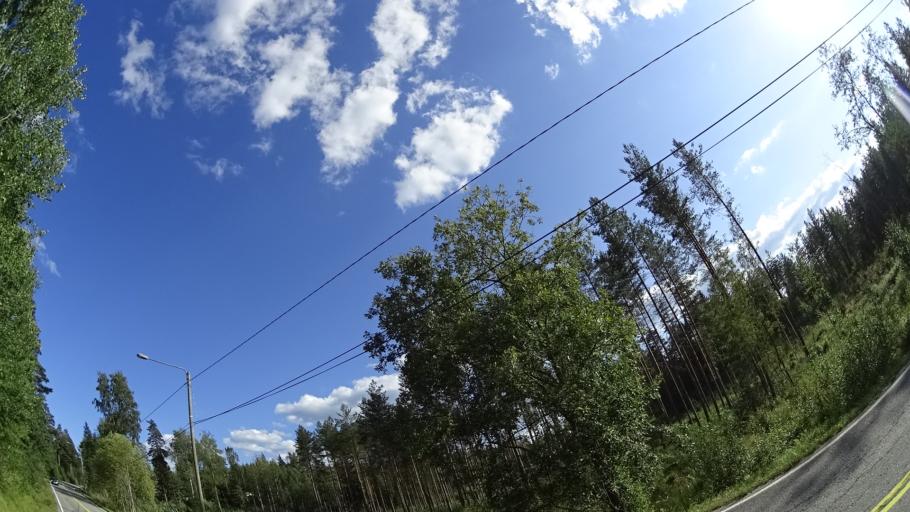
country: FI
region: Uusimaa
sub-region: Helsinki
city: Vihti
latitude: 60.3746
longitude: 24.3644
